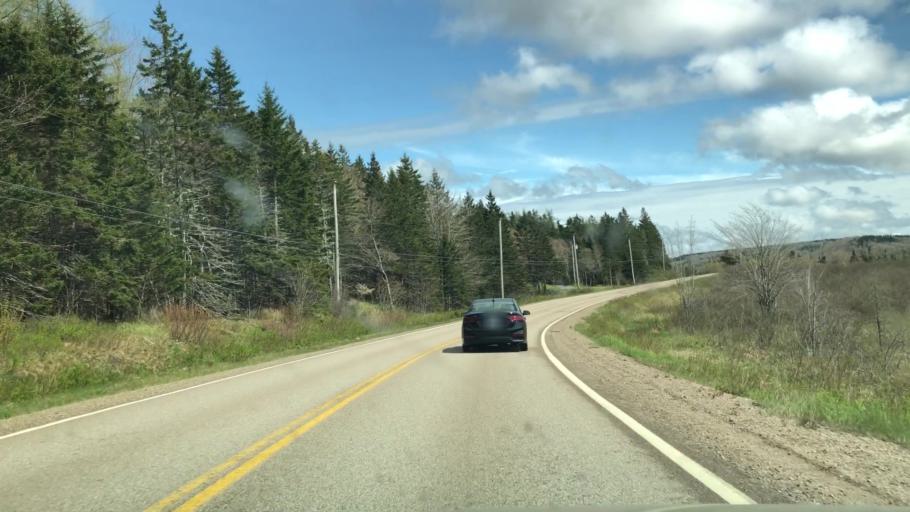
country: CA
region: Nova Scotia
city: Antigonish
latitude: 45.1908
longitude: -61.9903
